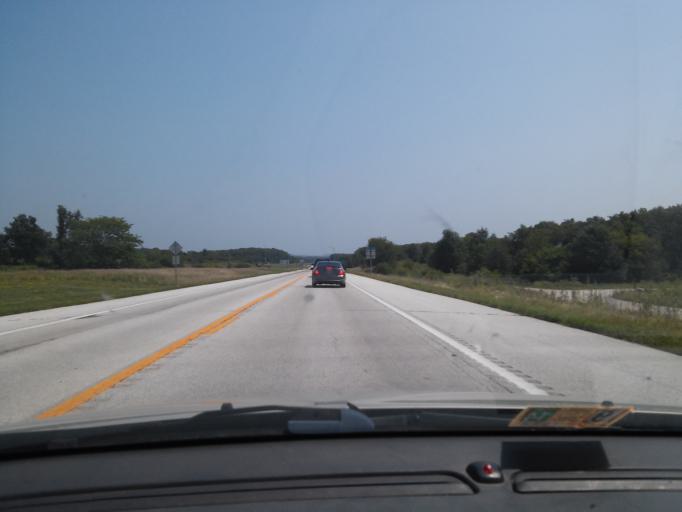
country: US
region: Missouri
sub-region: Pike County
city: Bowling Green
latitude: 39.3570
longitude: -91.2097
